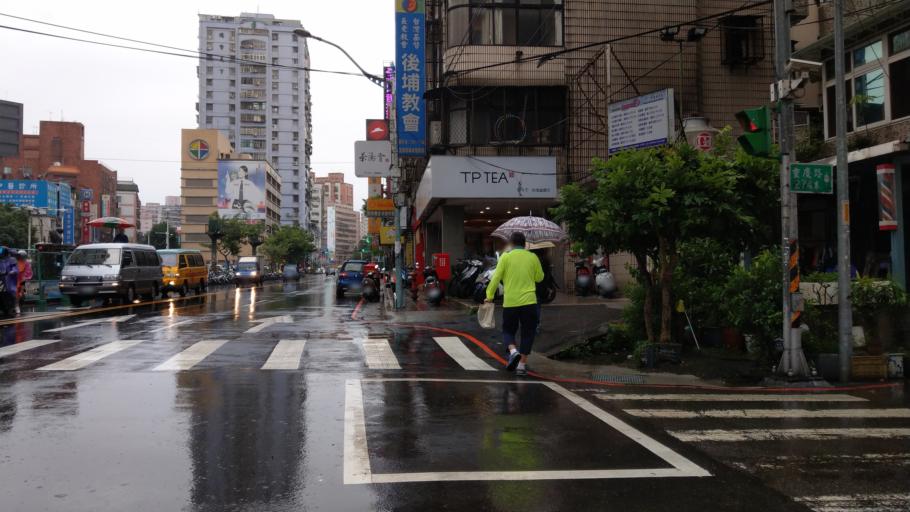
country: TW
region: Taipei
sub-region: Taipei
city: Banqiao
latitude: 25.0005
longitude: 121.4629
